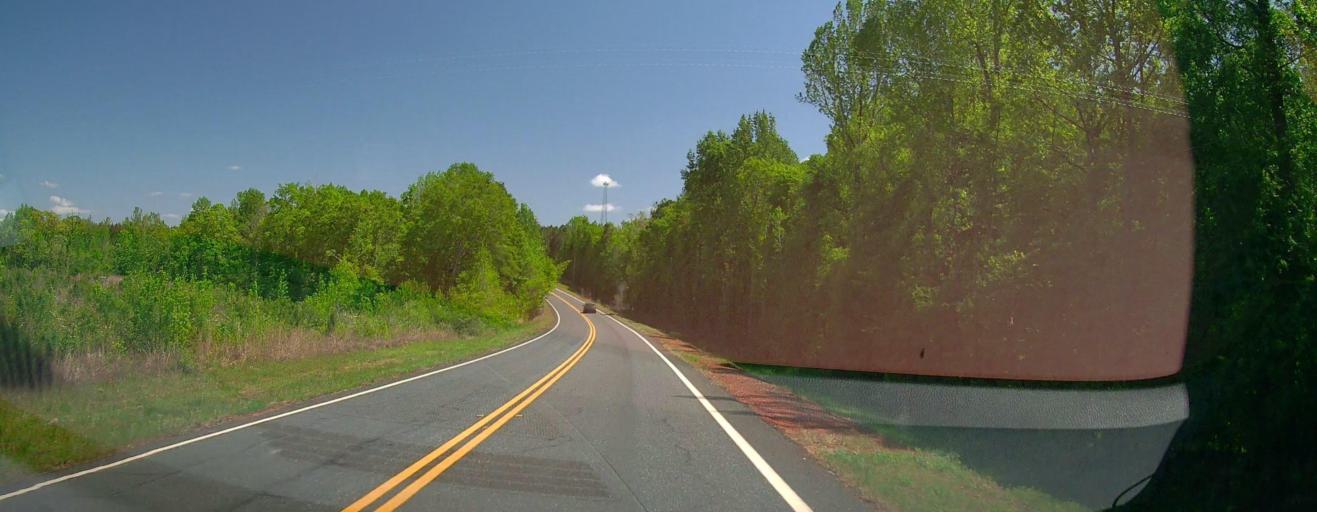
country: US
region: Georgia
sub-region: Jasper County
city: Monticello
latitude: 33.2381
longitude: -83.5502
